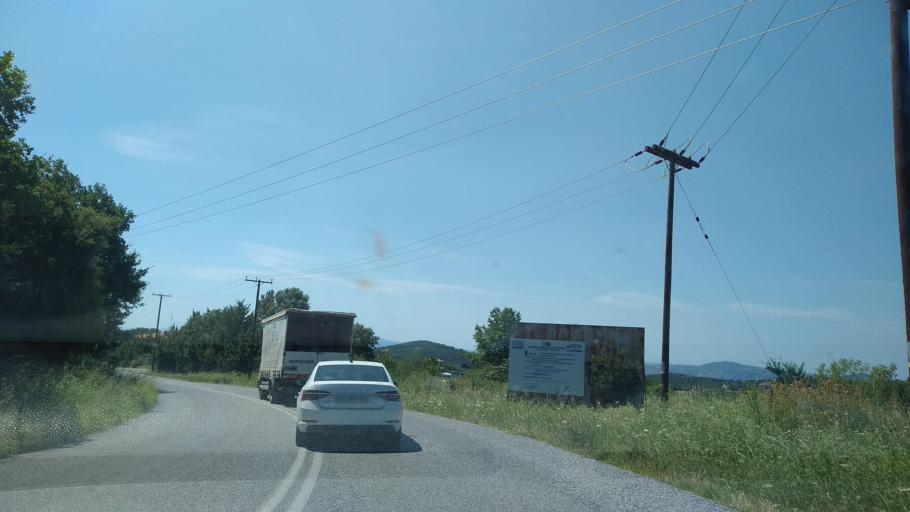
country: GR
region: Central Macedonia
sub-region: Nomos Chalkidikis
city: Megali Panagia
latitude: 40.4400
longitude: 23.6729
